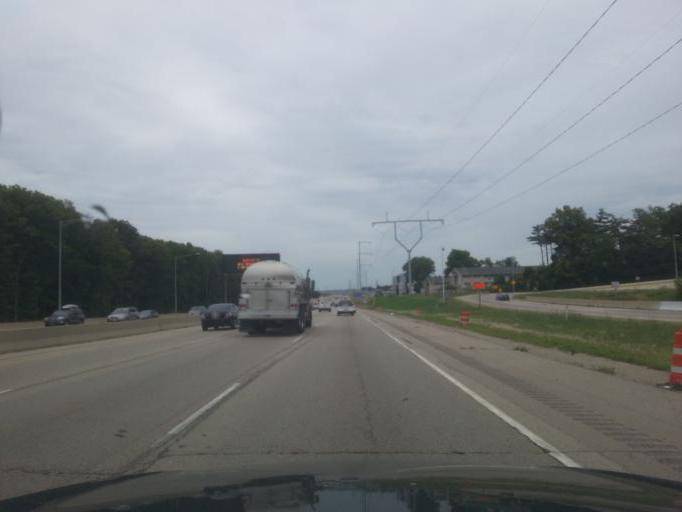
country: US
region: Wisconsin
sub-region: Dane County
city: Shorewood Hills
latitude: 43.0354
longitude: -89.4292
